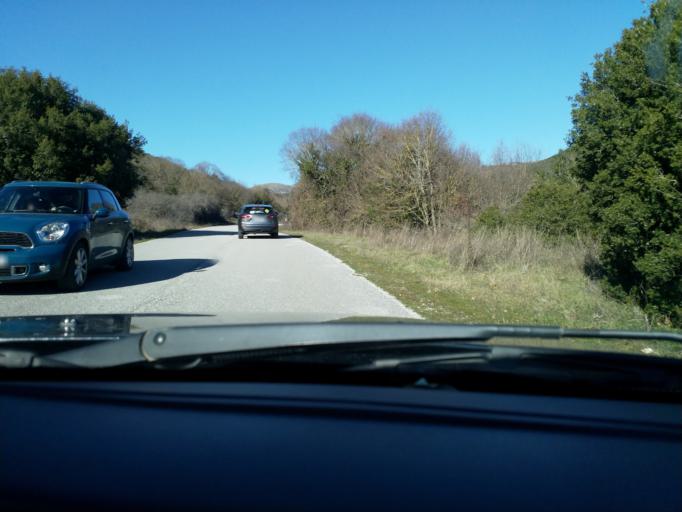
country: GR
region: Epirus
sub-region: Nomos Ioanninon
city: Kalpaki
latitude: 39.8914
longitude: 20.6711
